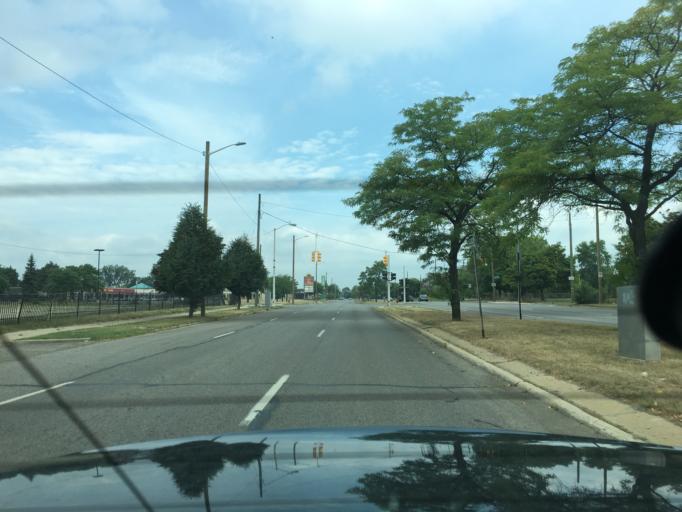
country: US
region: Michigan
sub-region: Wayne County
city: Highland Park
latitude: 42.3702
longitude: -83.0952
